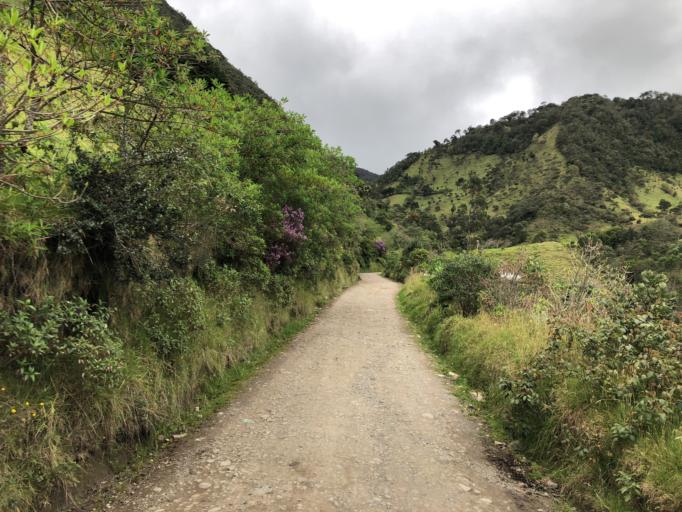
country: CO
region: Cauca
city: Totoro
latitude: 2.5089
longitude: -76.3638
